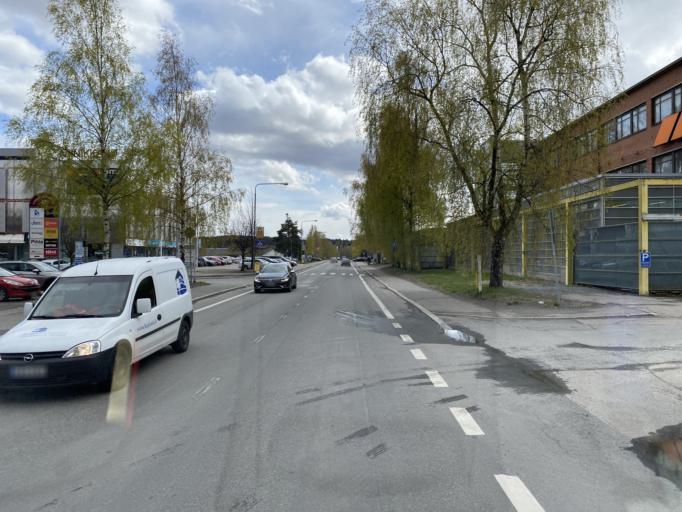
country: FI
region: Pirkanmaa
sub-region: Tampere
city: Tampere
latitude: 61.4813
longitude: 23.7826
